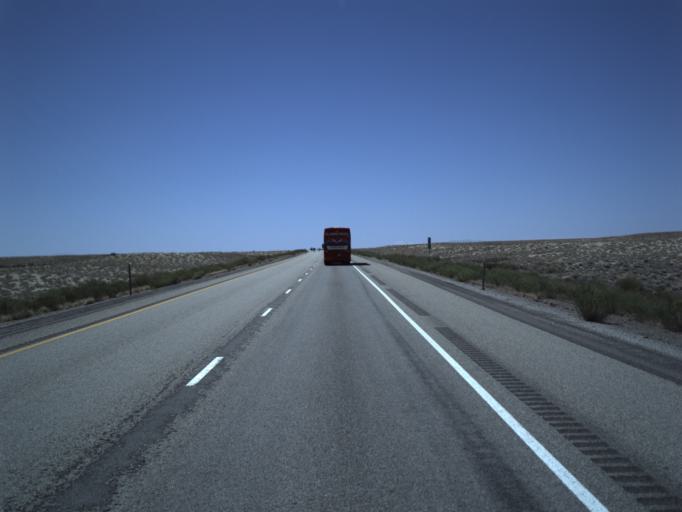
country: US
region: Utah
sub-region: Grand County
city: Moab
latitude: 38.9626
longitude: -109.3780
